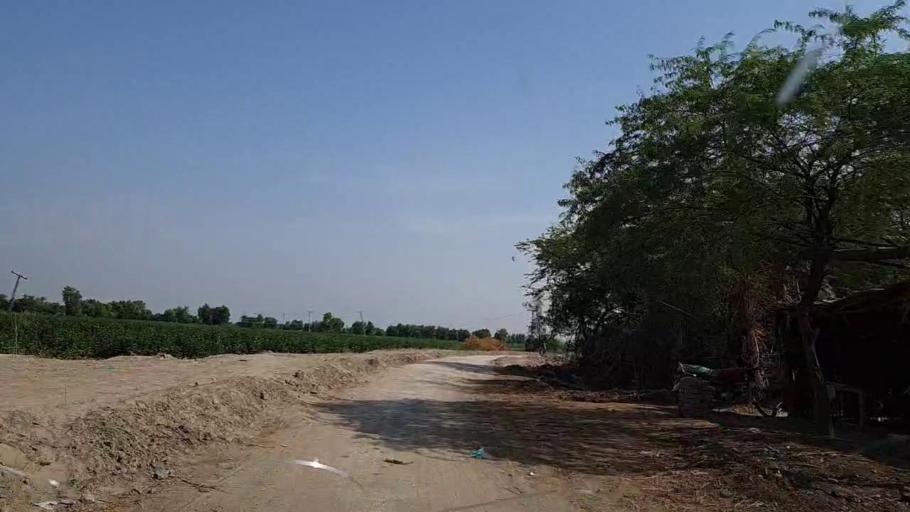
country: PK
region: Sindh
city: Khanpur
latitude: 27.7475
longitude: 69.3411
